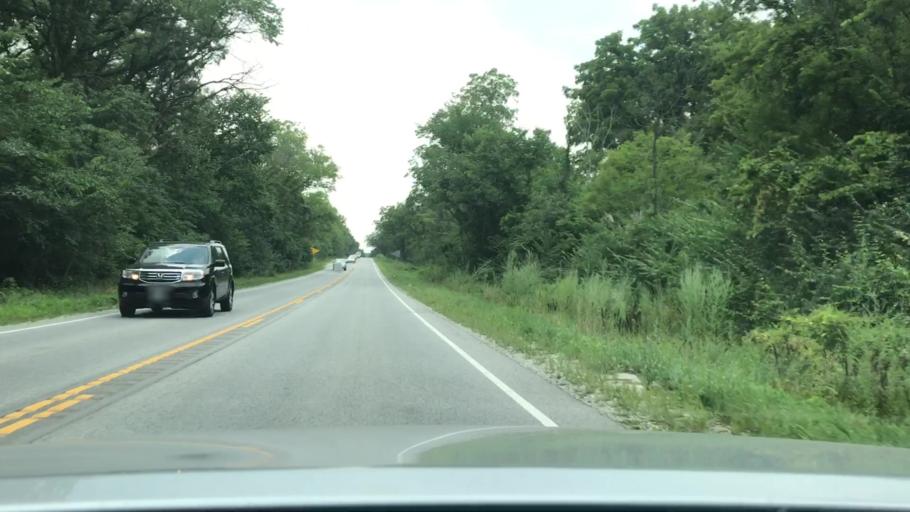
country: US
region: Illinois
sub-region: Cook County
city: Willow Springs
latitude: 41.6879
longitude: -87.8941
